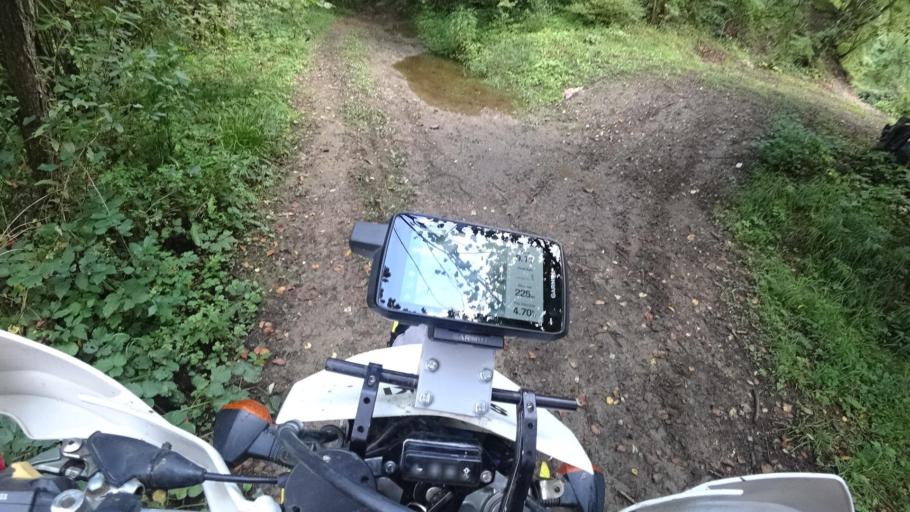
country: BA
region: Republika Srpska
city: Hiseti
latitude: 44.7737
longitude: 17.1256
